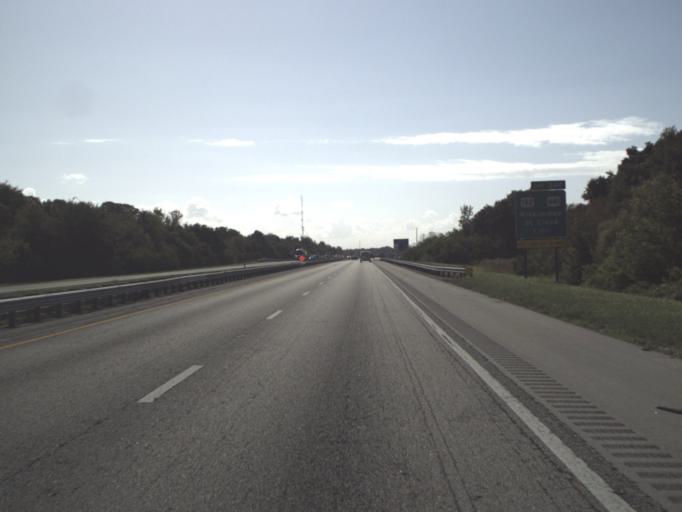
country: US
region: Florida
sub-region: Osceola County
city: Buenaventura Lakes
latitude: 28.3032
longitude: -81.3613
